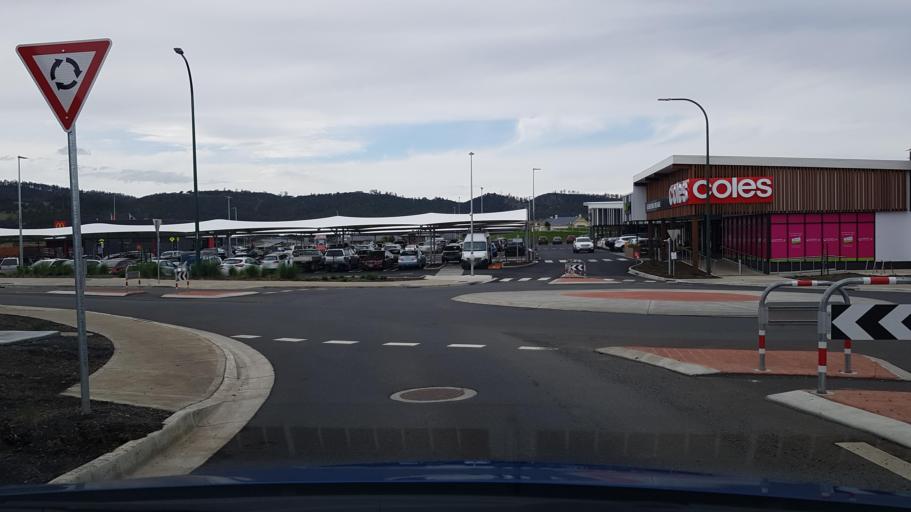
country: AU
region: Tasmania
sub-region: Clarence
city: Howrah
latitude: -42.8875
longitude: 147.4264
